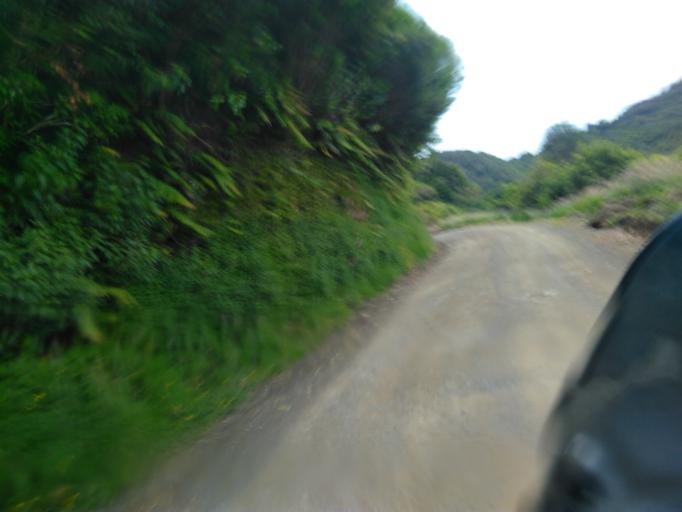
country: NZ
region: Bay of Plenty
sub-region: Opotiki District
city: Opotiki
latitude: -38.0928
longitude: 177.4855
